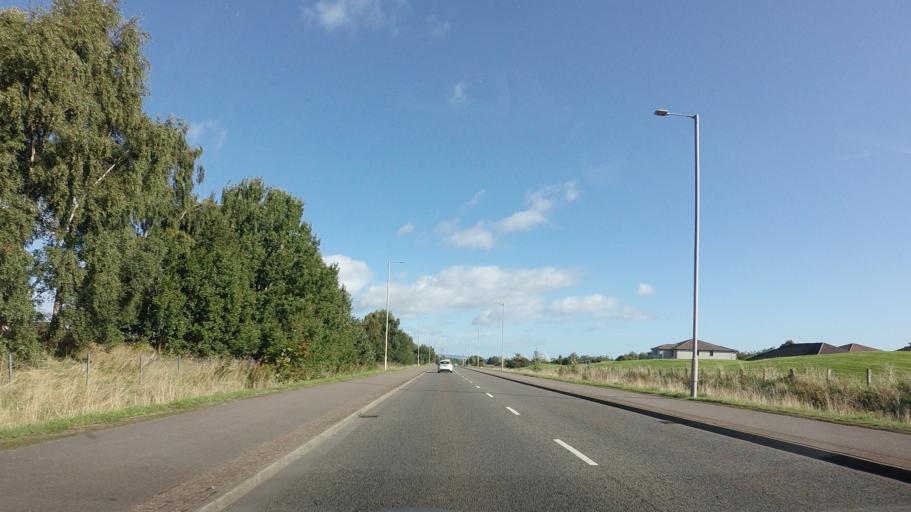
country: GB
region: Scotland
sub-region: Highland
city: Inverness
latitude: 57.4624
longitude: -4.1972
